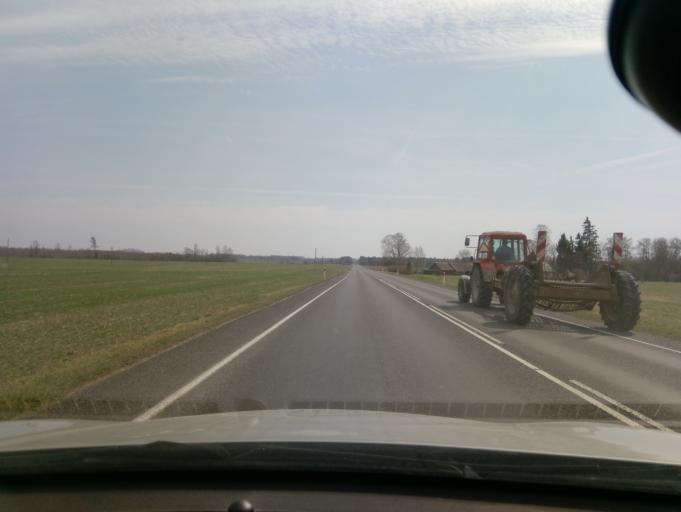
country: EE
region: Viljandimaa
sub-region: Vohma linn
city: Vohma
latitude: 58.7531
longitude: 25.5644
